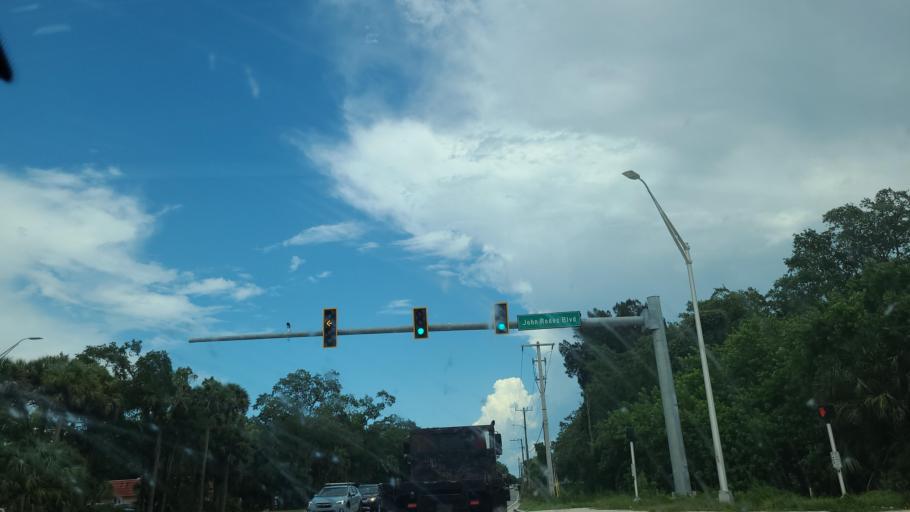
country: US
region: Florida
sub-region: Brevard County
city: June Park
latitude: 28.0989
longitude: -80.7004
